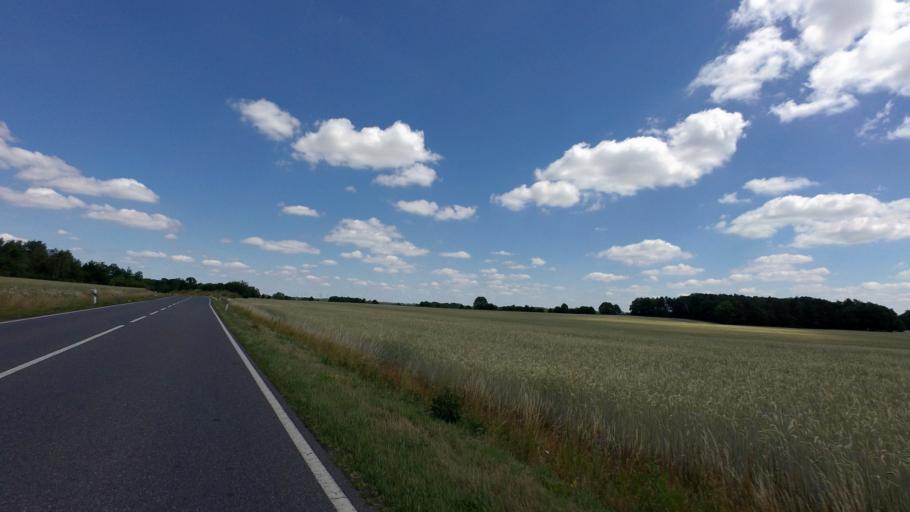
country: DE
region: Brandenburg
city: Luckau
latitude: 51.8257
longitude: 13.6847
